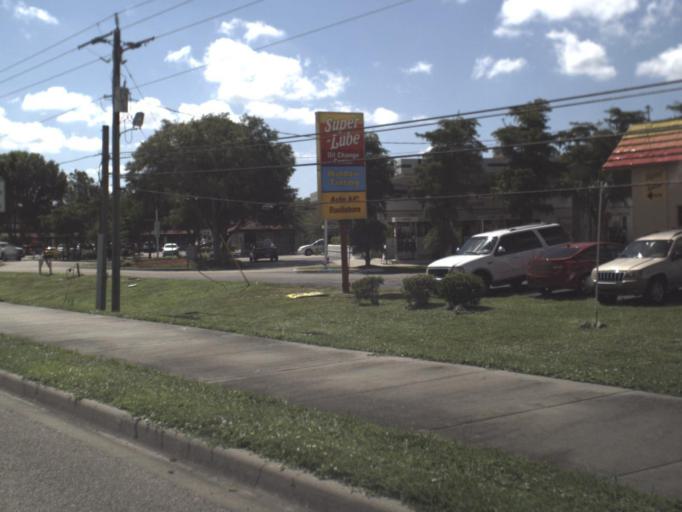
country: US
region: Florida
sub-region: Lee County
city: Villas
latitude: 26.5229
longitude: -81.8704
